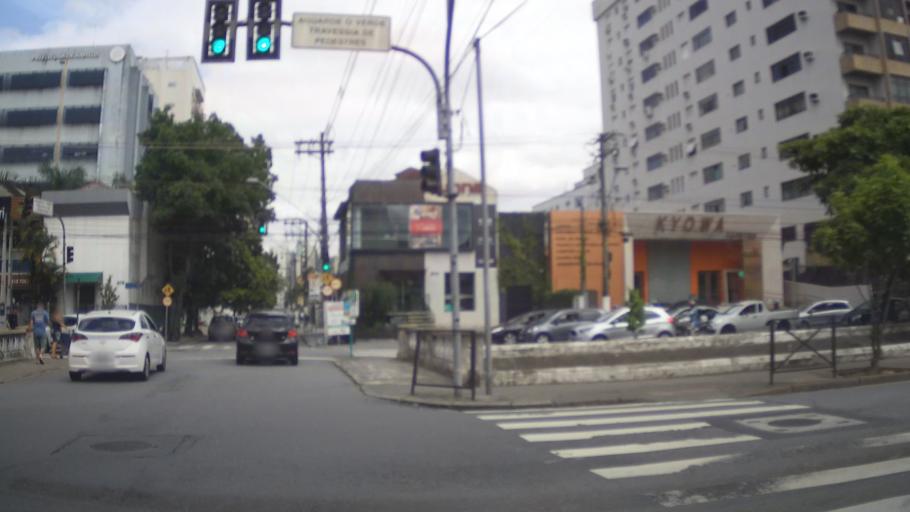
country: BR
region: Sao Paulo
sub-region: Santos
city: Santos
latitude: -23.9609
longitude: -46.3279
